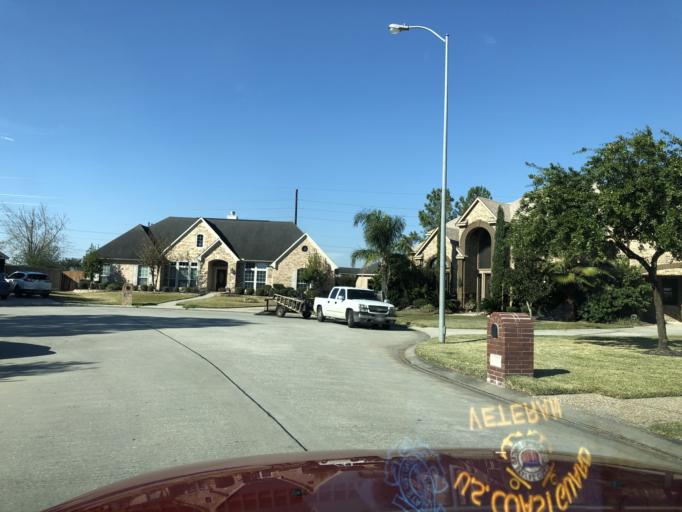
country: US
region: Texas
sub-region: Harris County
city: Tomball
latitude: 30.0371
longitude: -95.5488
